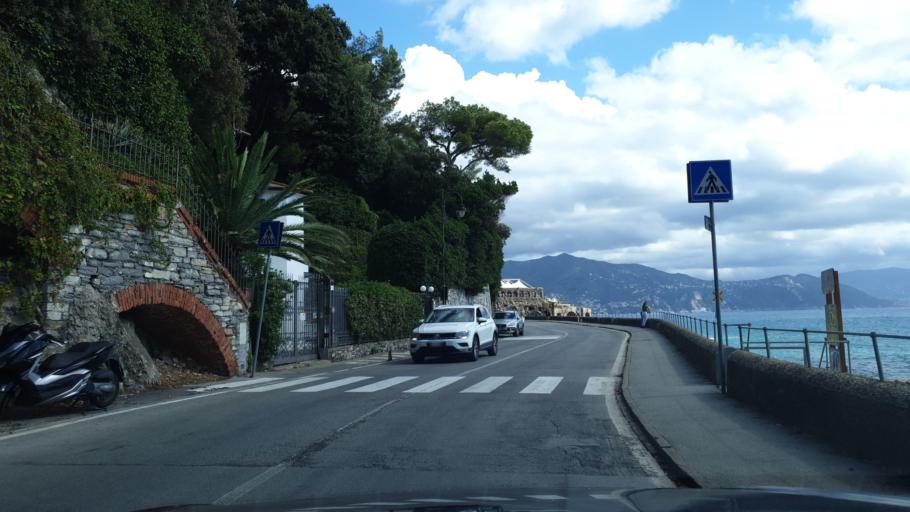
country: IT
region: Liguria
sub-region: Provincia di Genova
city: Santa Margherita Ligure
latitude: 44.3204
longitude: 9.2129
